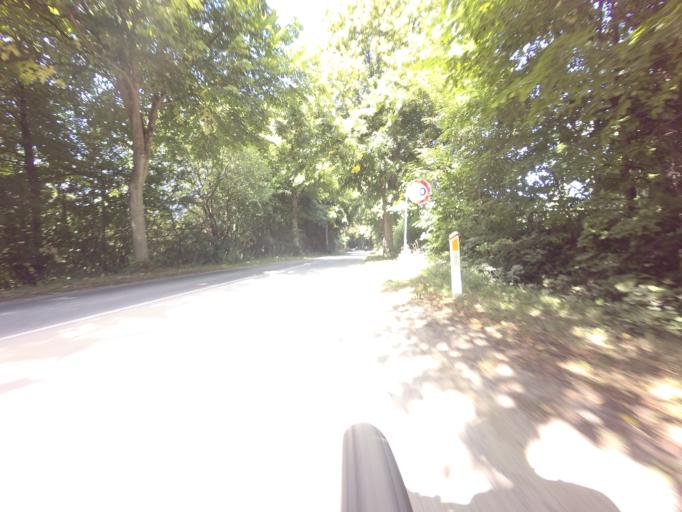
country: DK
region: Zealand
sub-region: Vordingborg Kommune
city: Stege
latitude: 54.9779
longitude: 12.5252
